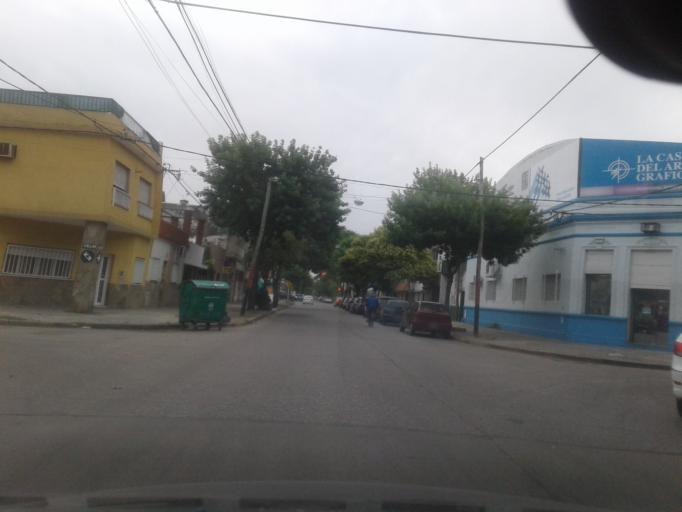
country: AR
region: Santa Fe
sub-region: Departamento de Rosario
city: Rosario
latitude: -32.9649
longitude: -60.6655
